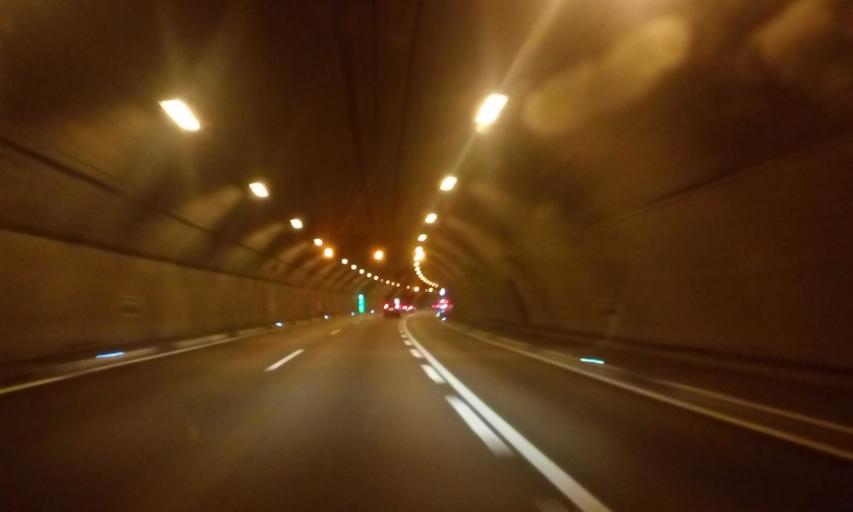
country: CH
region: Bern
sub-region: Bern-Mittelland District
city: Wohlen
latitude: 46.9485
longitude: 7.3822
